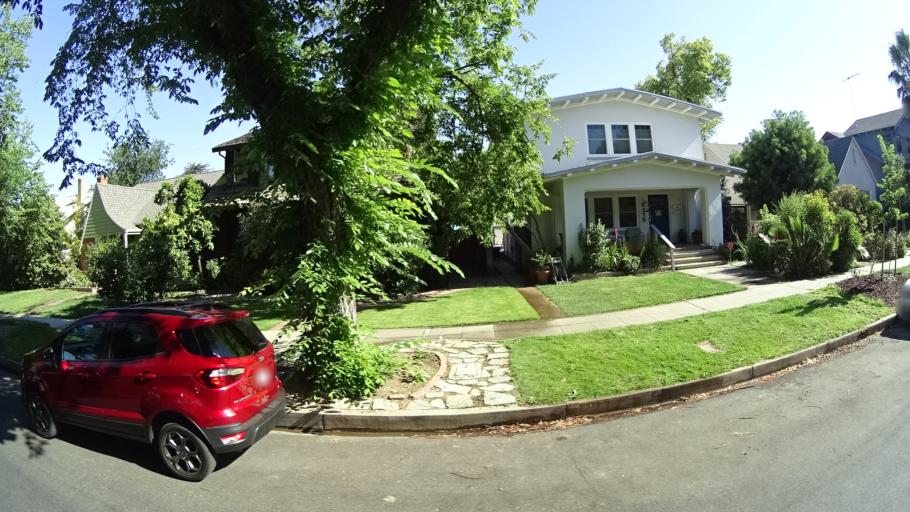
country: US
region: California
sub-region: Sacramento County
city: Sacramento
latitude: 38.5524
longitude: -121.4867
